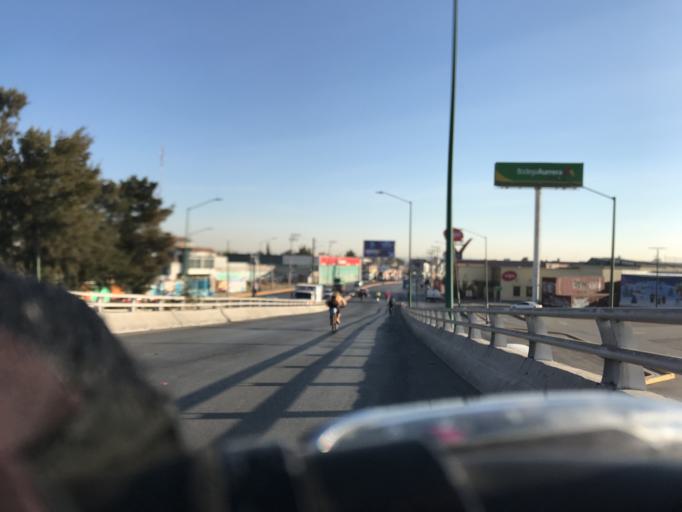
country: MX
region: Mexico
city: Cuautitlan
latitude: 19.6706
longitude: -99.1755
